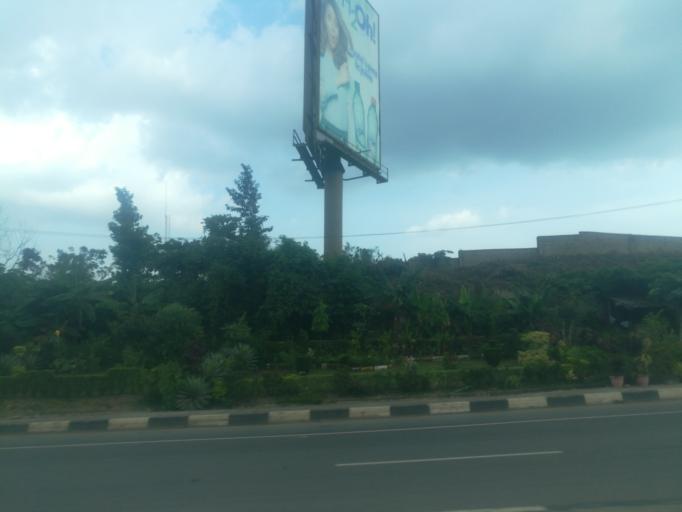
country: NG
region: Oyo
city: Ibadan
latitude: 7.3333
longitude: 3.8742
